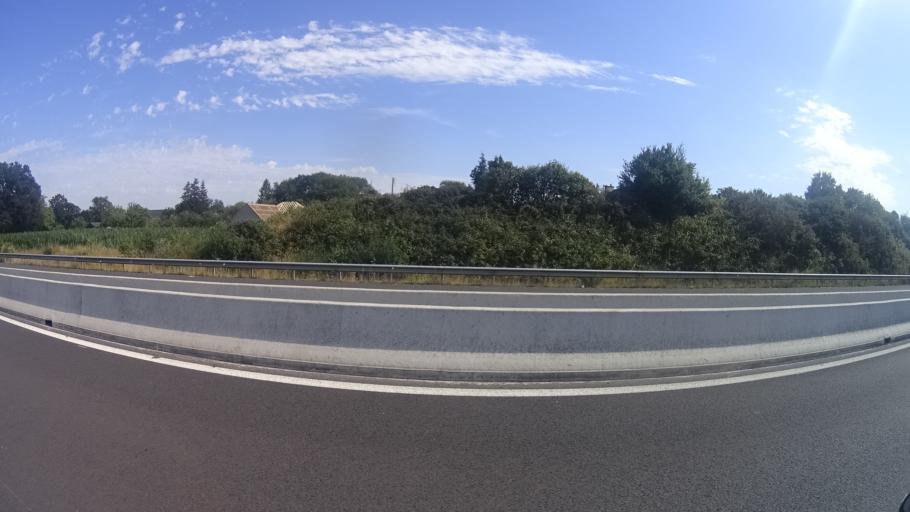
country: FR
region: Brittany
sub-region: Departement du Morbihan
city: Saint-Jean-la-Poterie
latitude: 47.6200
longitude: -2.1087
